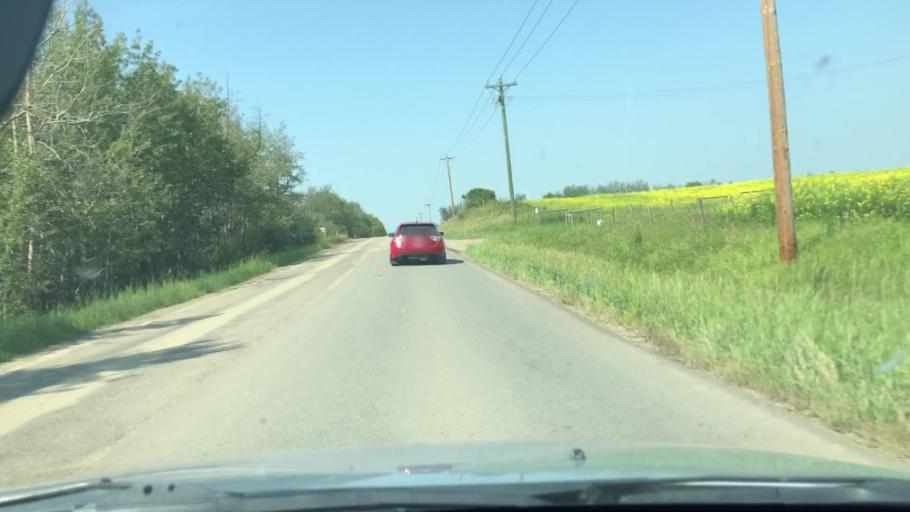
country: CA
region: Alberta
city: Devon
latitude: 53.5122
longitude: -113.7457
